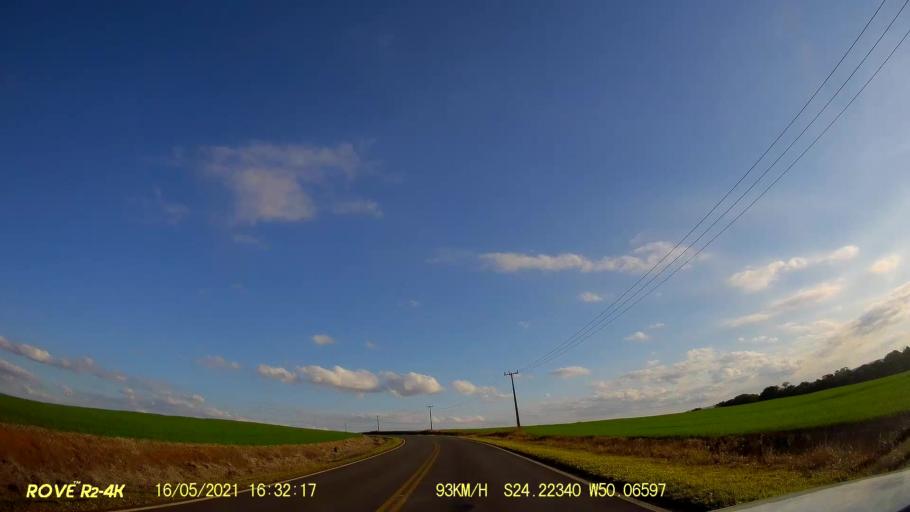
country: BR
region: Parana
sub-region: Pirai Do Sul
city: Pirai do Sul
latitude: -24.2244
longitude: -50.0662
